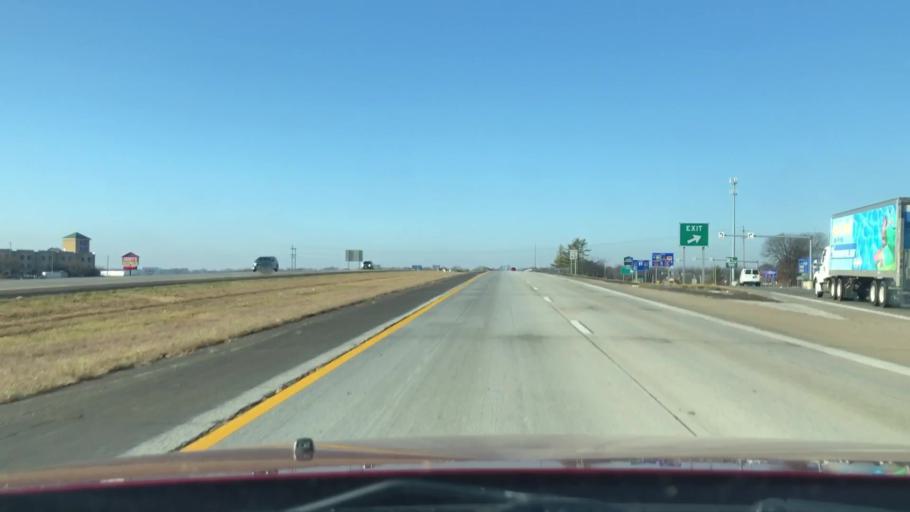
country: US
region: Missouri
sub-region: Greene County
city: Springfield
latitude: 37.1376
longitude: -93.2927
